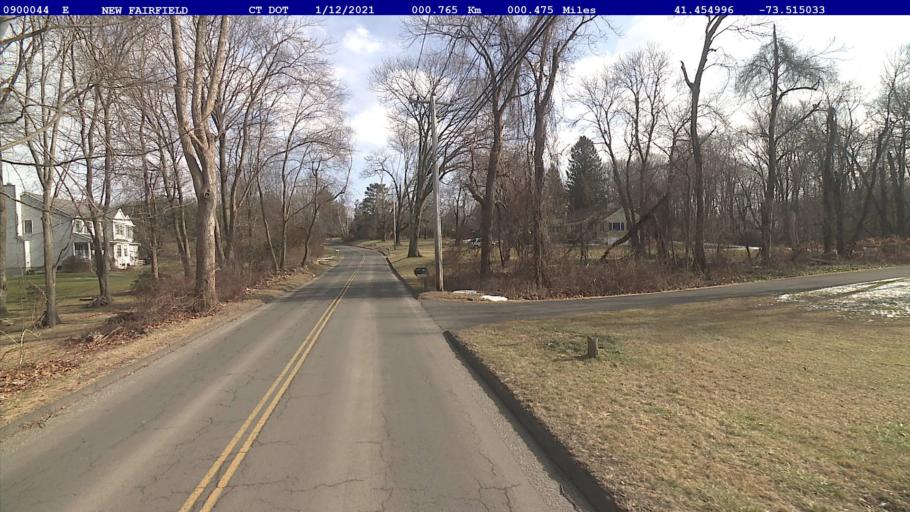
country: US
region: New York
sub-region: Putnam County
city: Putnam Lake
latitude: 41.4550
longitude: -73.5150
